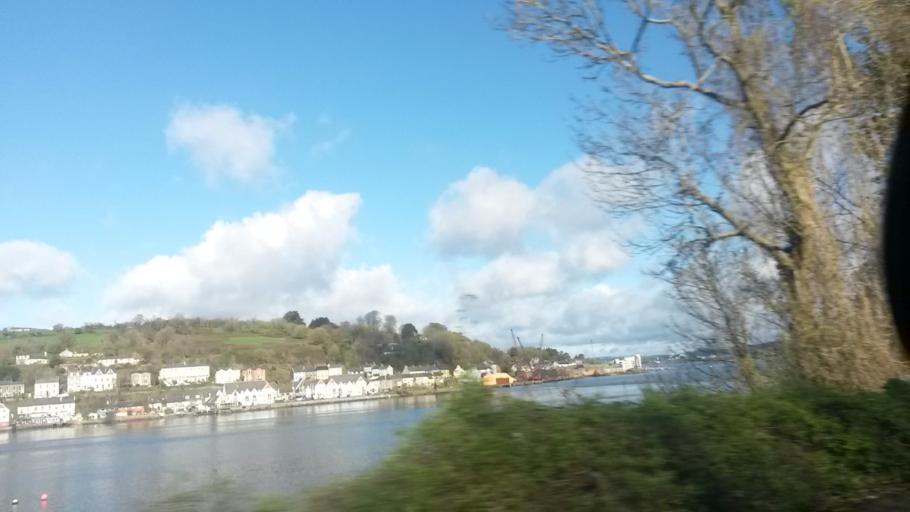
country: IE
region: Munster
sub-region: County Cork
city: Passage West
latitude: 51.8642
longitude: -8.3258
